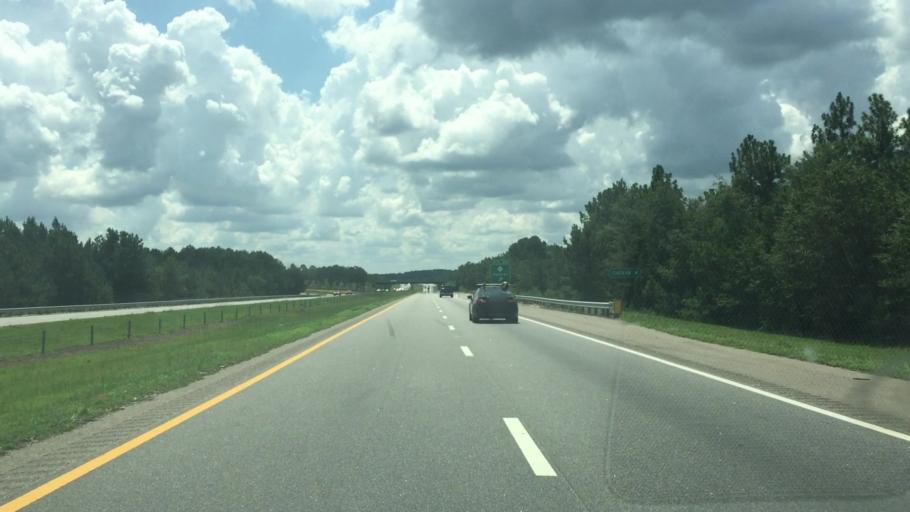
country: US
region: North Carolina
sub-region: Richmond County
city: East Rockingham
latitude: 34.8632
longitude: -79.7487
